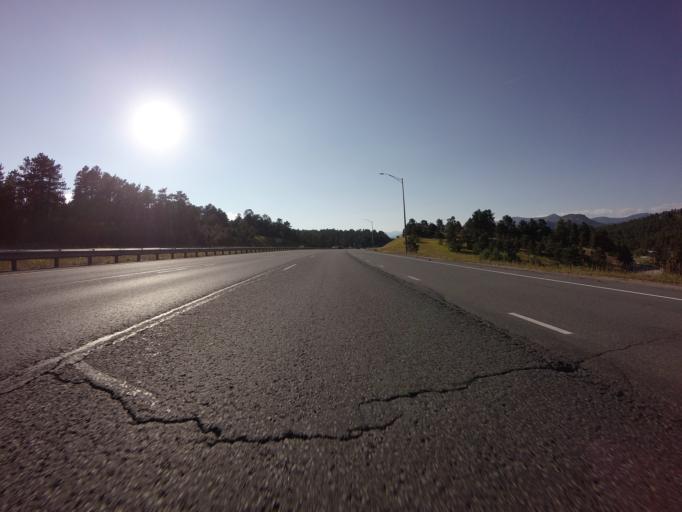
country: US
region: Colorado
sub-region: Jefferson County
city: Kittredge
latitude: 39.7043
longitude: -105.3423
